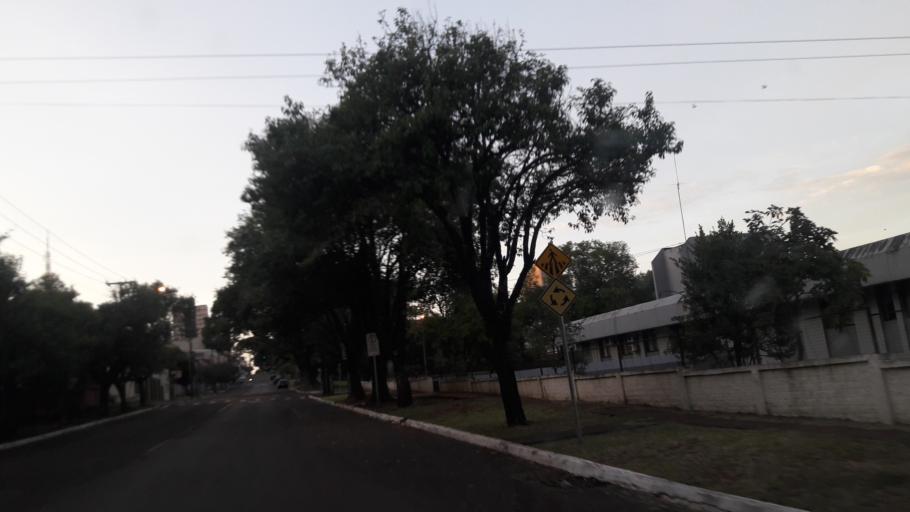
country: BR
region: Parana
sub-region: Cascavel
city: Cascavel
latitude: -24.9563
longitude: -53.4495
